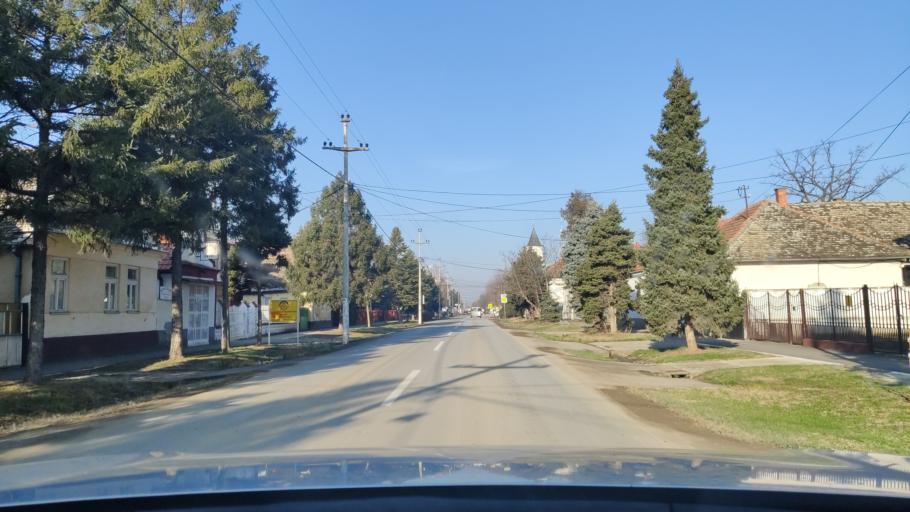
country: RS
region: Central Serbia
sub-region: Belgrade
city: Surcin
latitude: 44.7525
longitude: 20.2617
